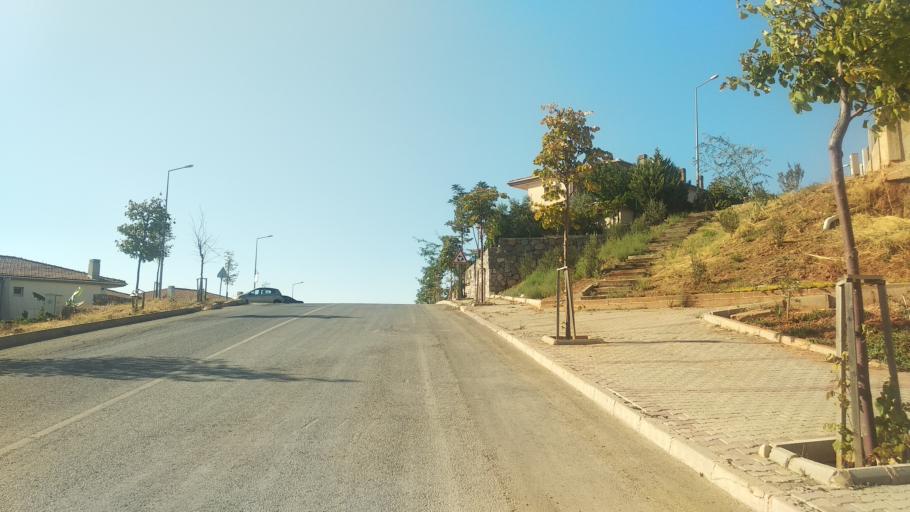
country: TR
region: Izmir
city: Urla
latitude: 38.3590
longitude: 26.8803
